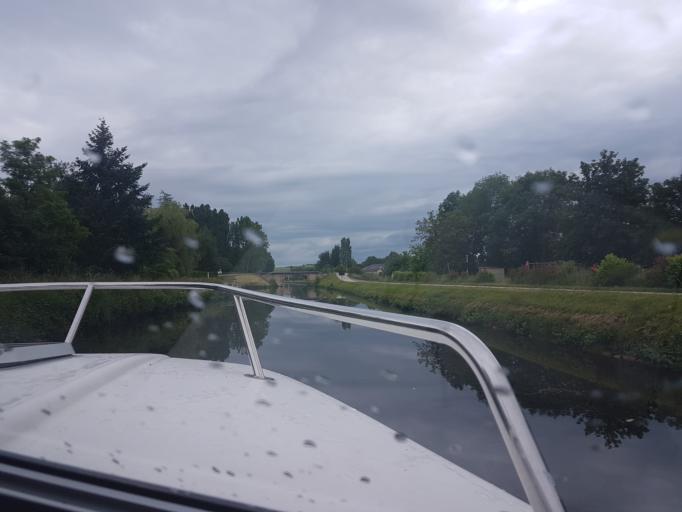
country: FR
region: Bourgogne
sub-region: Departement de l'Yonne
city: Saint-Bris-le-Vineux
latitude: 47.7077
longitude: 3.6364
